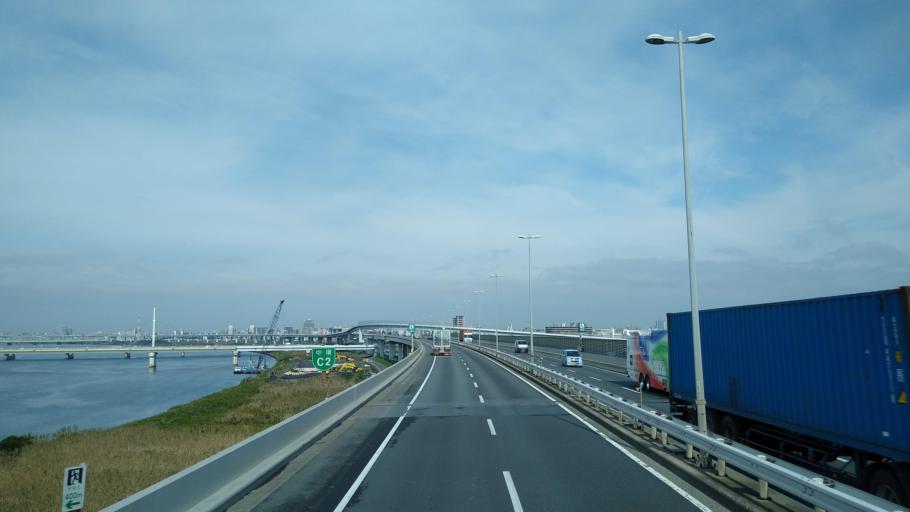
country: JP
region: Tokyo
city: Urayasu
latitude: 35.6914
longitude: 139.8622
